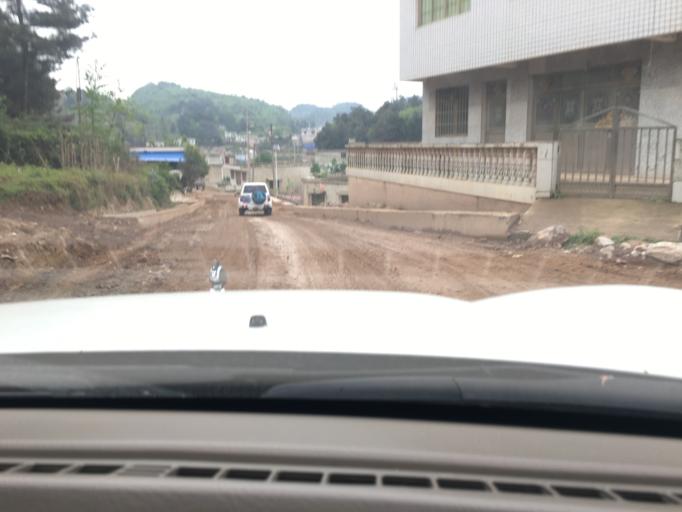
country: CN
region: Guizhou Sheng
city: Supu
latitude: 26.7346
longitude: 106.4369
